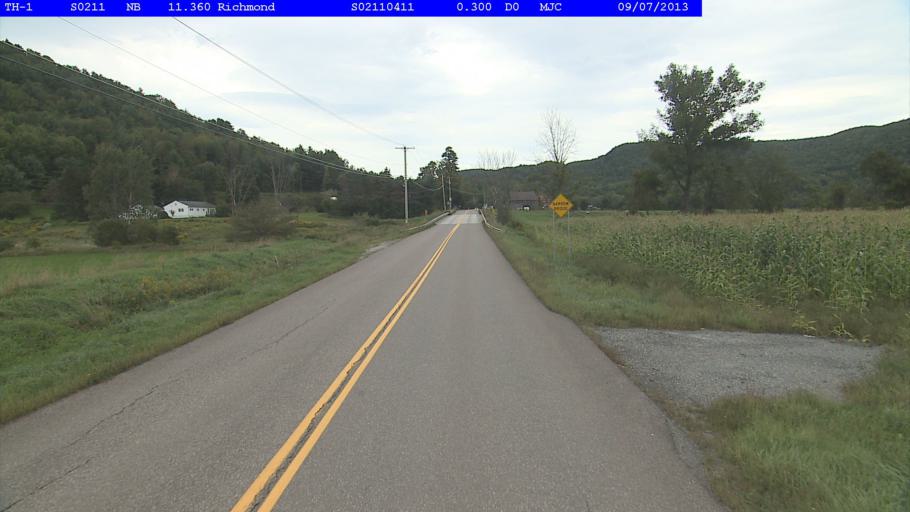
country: US
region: Vermont
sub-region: Chittenden County
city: Williston
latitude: 44.3575
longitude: -72.9928
